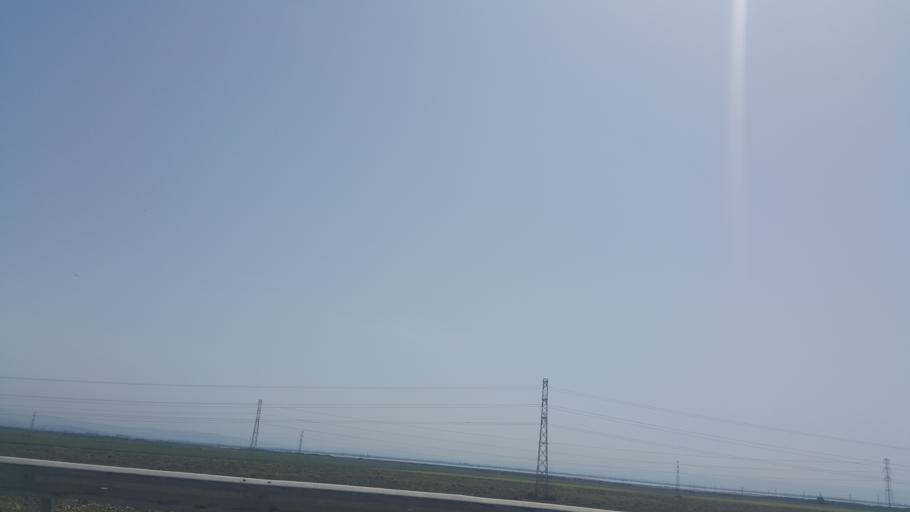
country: TR
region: Hatay
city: Serinyol
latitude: 36.4208
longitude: 36.2743
